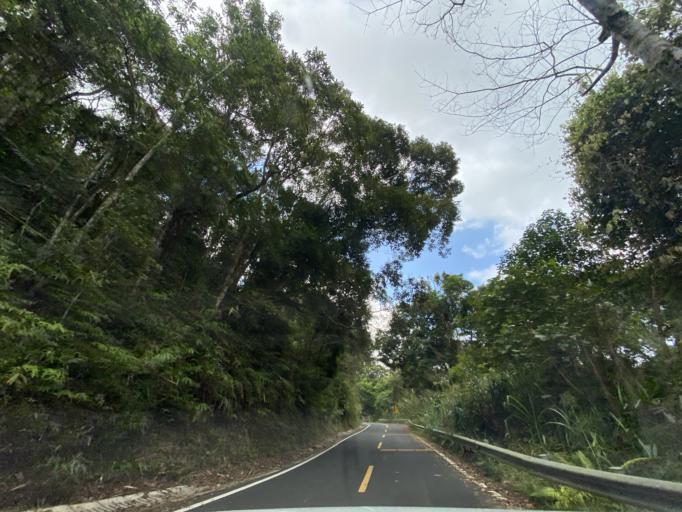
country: CN
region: Hainan
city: Diaoluoshan
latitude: 18.7072
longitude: 109.8827
